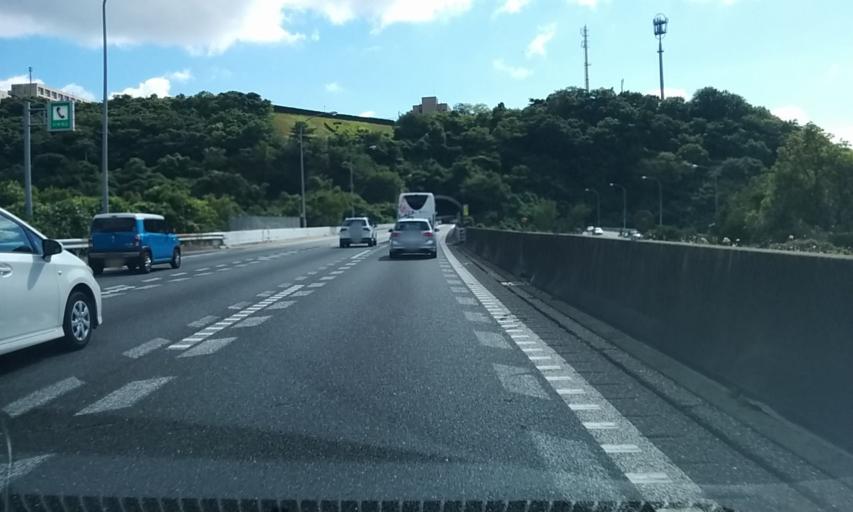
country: JP
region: Hyogo
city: Takarazuka
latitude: 34.8217
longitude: 135.3331
